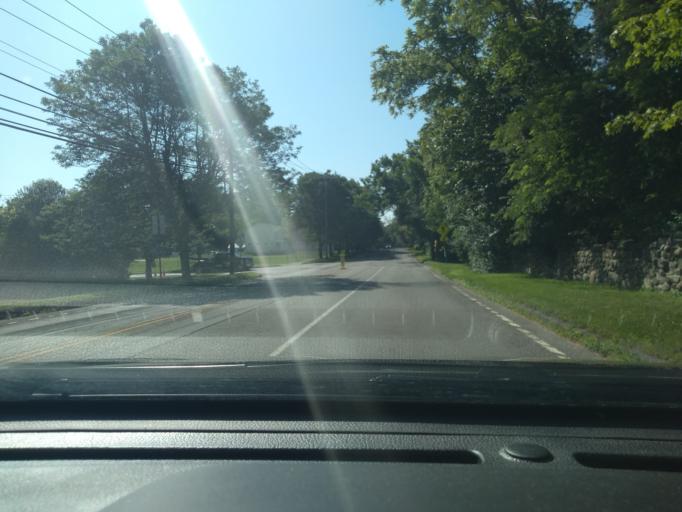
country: US
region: New York
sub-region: Erie County
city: Billington Heights
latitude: 42.7718
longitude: -78.6338
